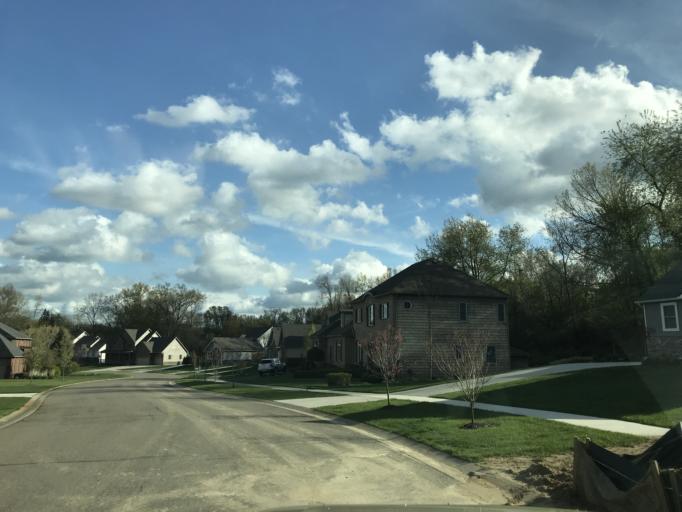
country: US
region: Michigan
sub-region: Livingston County
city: Brighton
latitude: 42.5392
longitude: -83.7578
